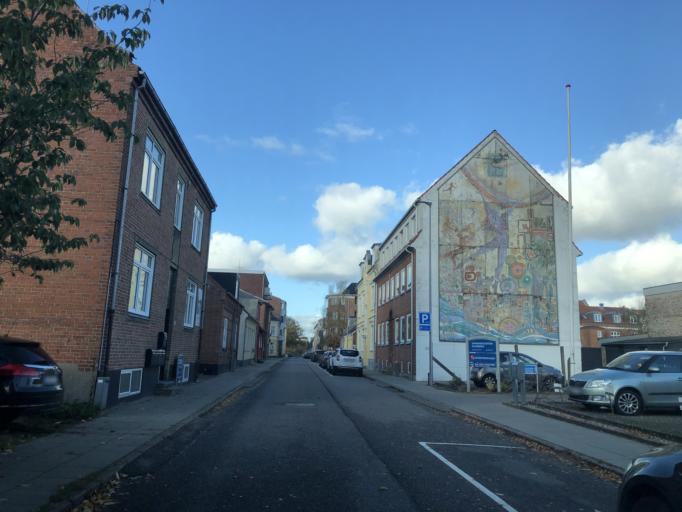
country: DK
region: Central Jutland
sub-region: Silkeborg Kommune
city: Silkeborg
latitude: 56.1648
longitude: 9.5415
